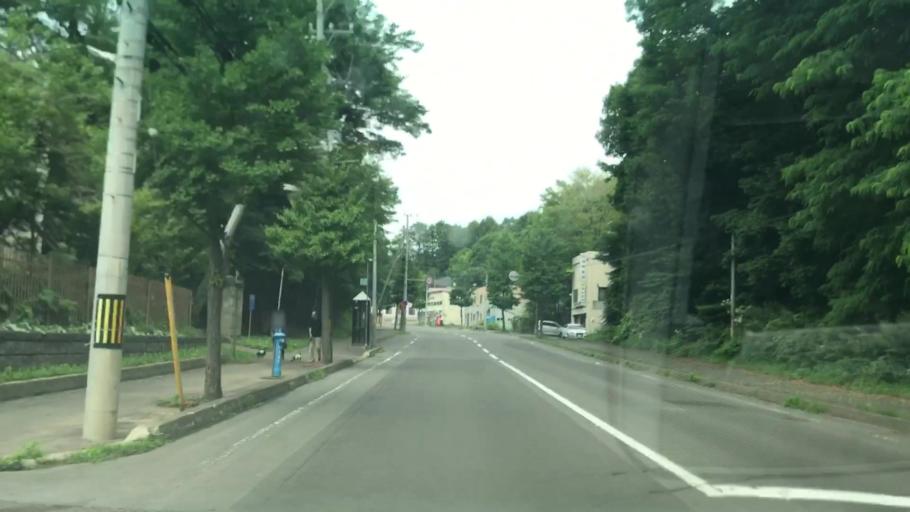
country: JP
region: Hokkaido
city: Otaru
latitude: 43.2111
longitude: 140.9671
